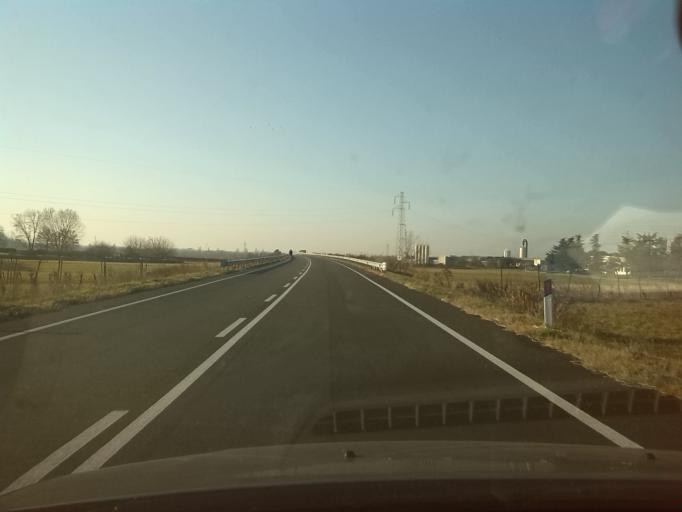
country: IT
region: Friuli Venezia Giulia
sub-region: Provincia di Udine
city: Manzano
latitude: 45.9774
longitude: 13.3658
